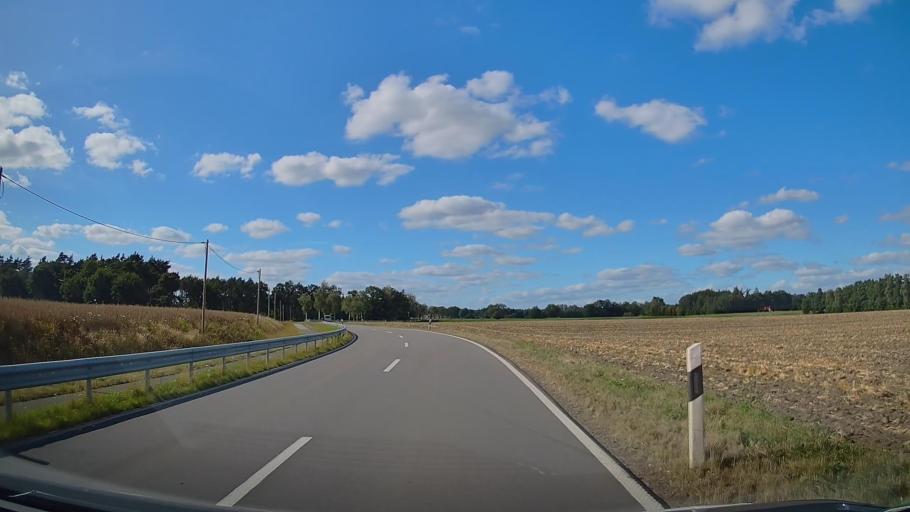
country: DE
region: Lower Saxony
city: Loningen
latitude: 52.6964
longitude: 7.7612
